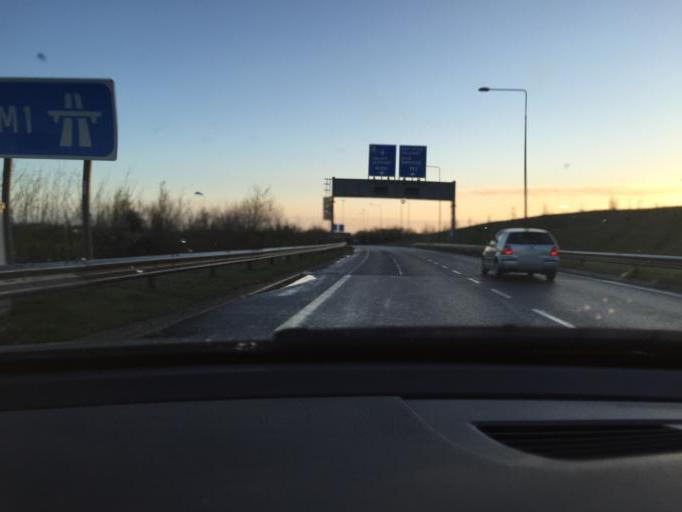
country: IE
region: Leinster
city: Beaumont
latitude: 53.4120
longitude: -6.2283
